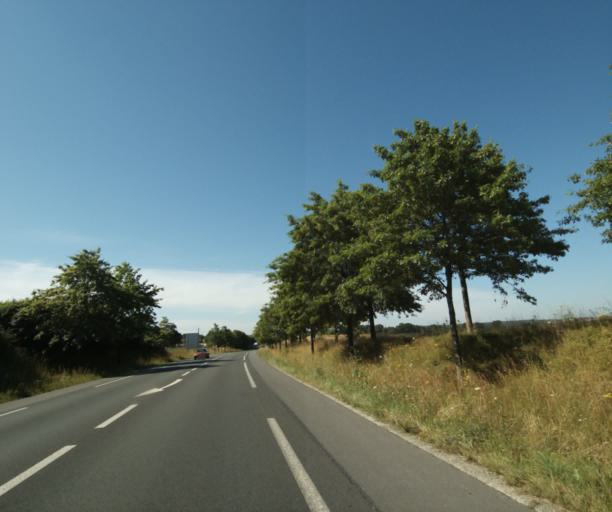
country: FR
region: Pays de la Loire
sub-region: Departement de la Mayenne
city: Bonchamp-les-Laval
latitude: 48.0702
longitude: -0.7307
